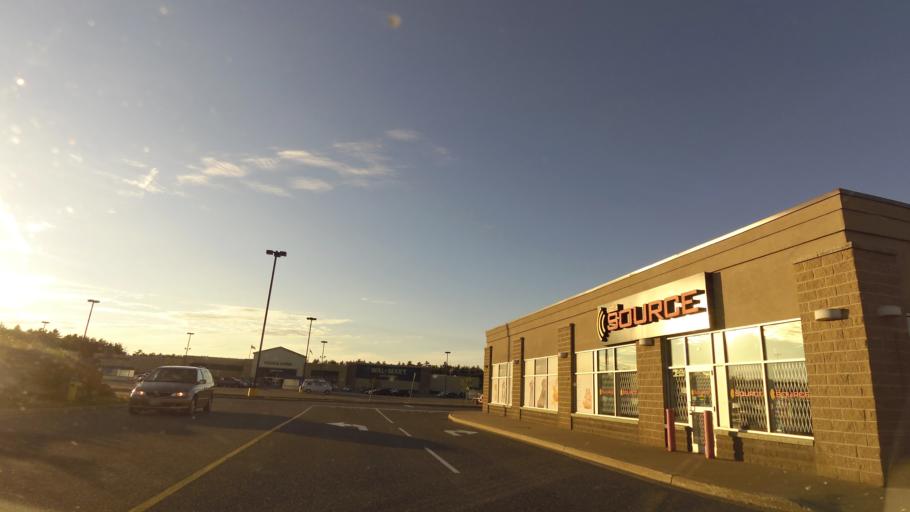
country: CA
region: Ontario
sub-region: Parry Sound District
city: Parry Sound
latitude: 45.3453
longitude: -80.0108
